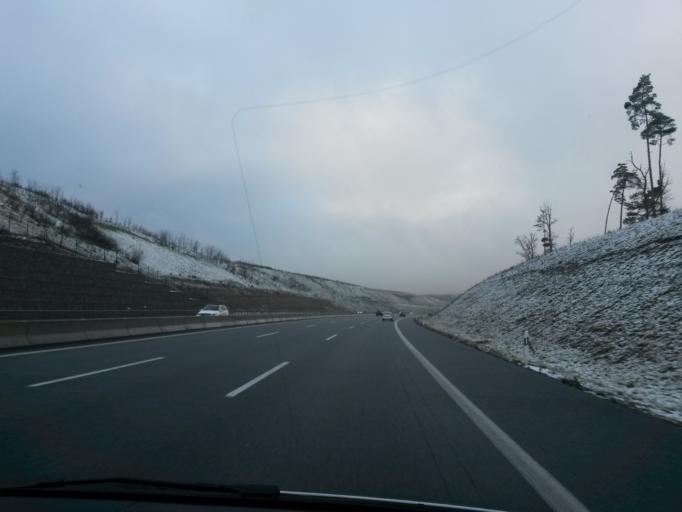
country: DE
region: Baden-Wuerttemberg
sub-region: Karlsruhe Region
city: Friolzheim
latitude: 48.8405
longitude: 8.8294
